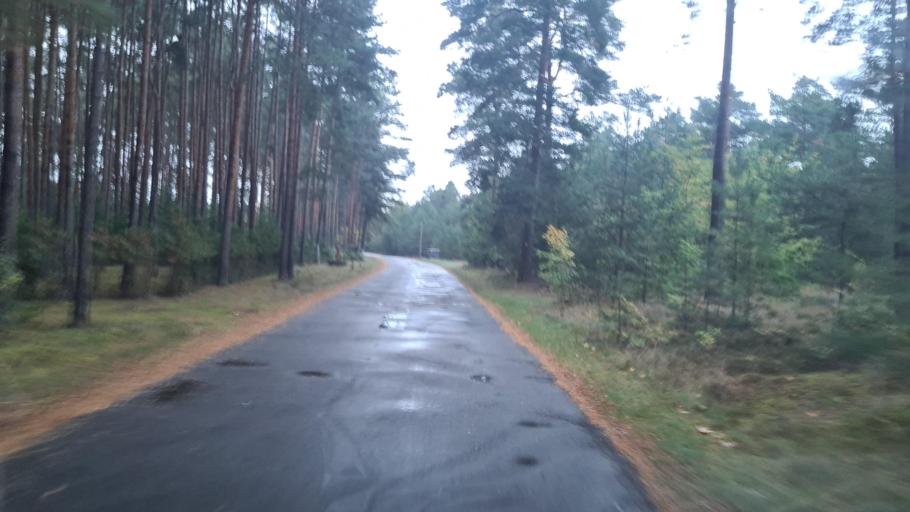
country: DE
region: Brandenburg
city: Munchehofe
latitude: 52.1342
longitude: 13.9420
